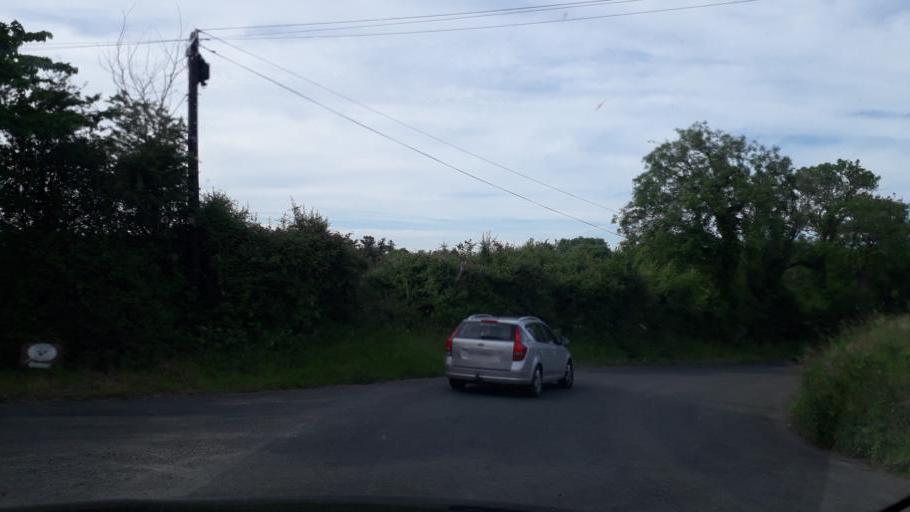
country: IE
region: Leinster
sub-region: Loch Garman
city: Courtown
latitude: 52.5449
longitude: -6.2550
